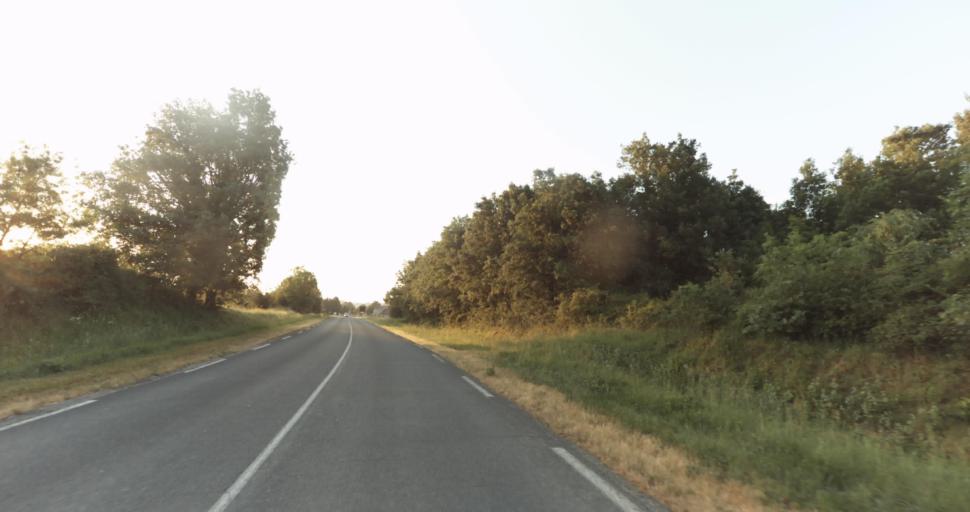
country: FR
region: Midi-Pyrenees
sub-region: Departement du Gers
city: Pujaudran
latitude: 43.6383
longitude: 1.1454
